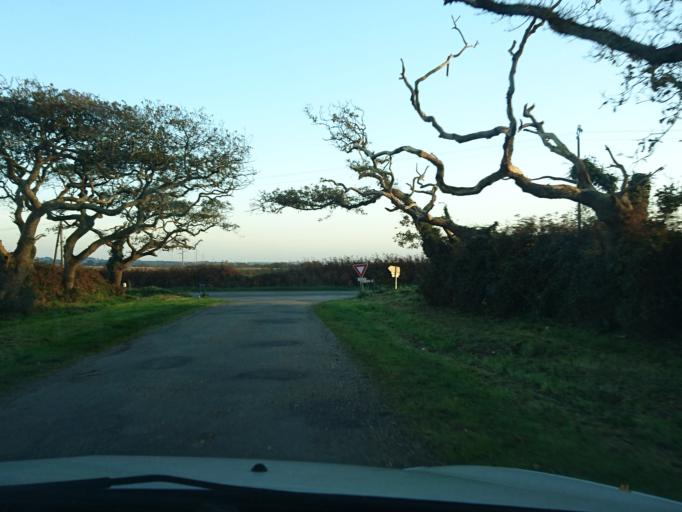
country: FR
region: Brittany
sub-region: Departement du Finistere
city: Lanrivoare
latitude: 48.4732
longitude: -4.6647
